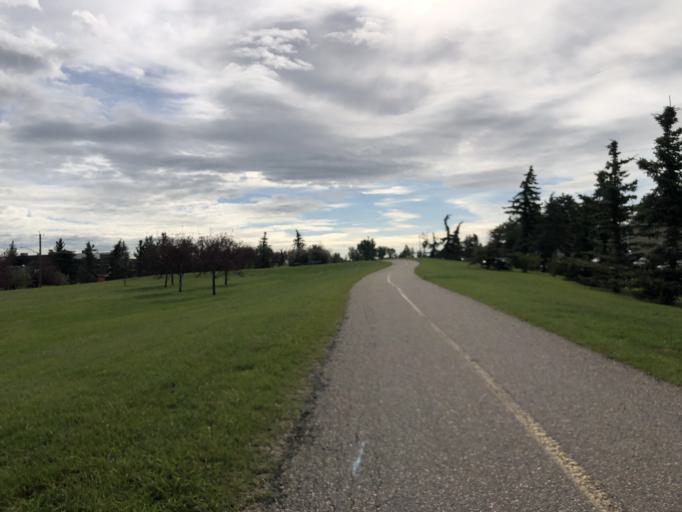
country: CA
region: Alberta
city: Calgary
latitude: 51.0745
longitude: -114.0163
